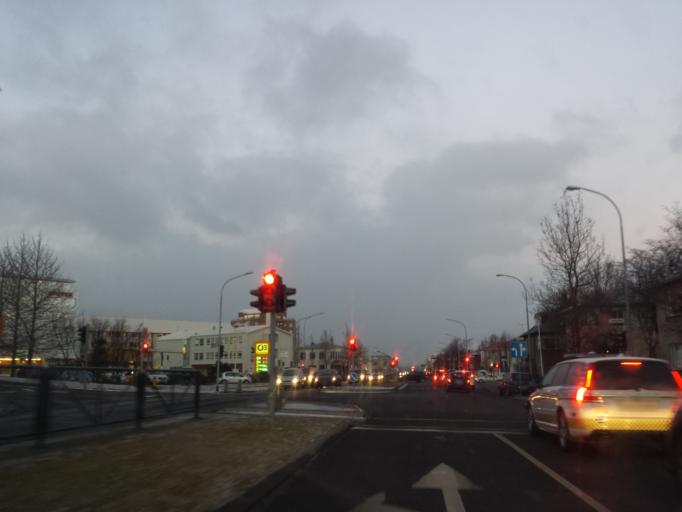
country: IS
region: Capital Region
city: Reykjavik
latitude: 64.1389
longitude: -21.9210
